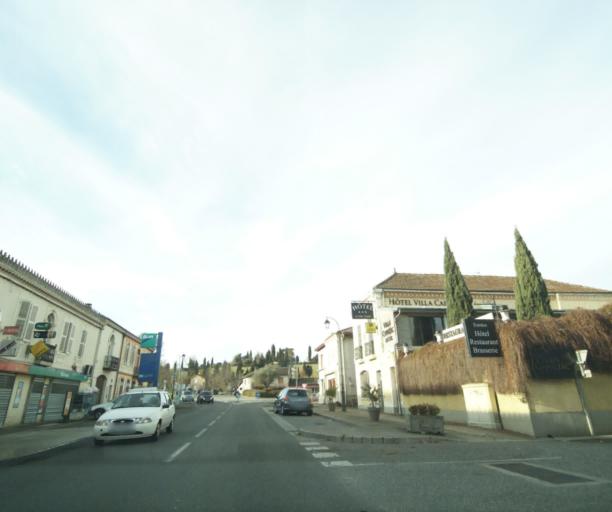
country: FR
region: Midi-Pyrenees
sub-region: Departement du Gers
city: Gimont
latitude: 43.6311
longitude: 0.8672
